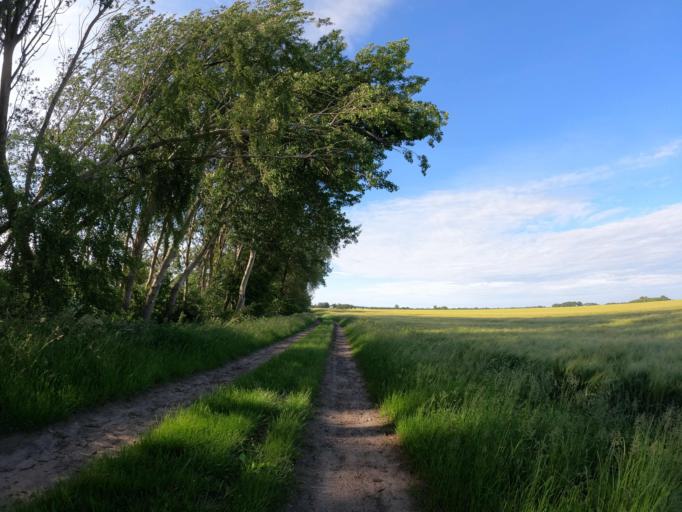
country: DE
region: Mecklenburg-Vorpommern
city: Preetz
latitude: 54.3231
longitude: 12.9737
